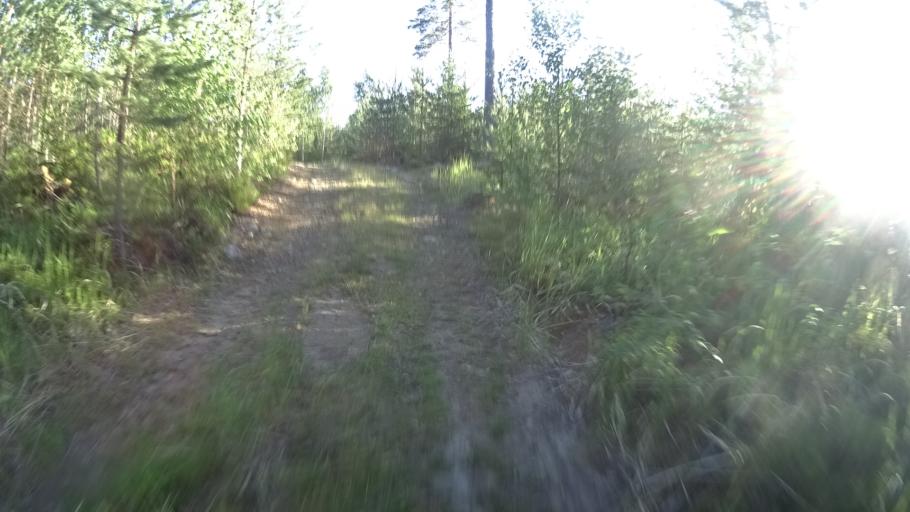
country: FI
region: Uusimaa
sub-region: Helsinki
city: Karkkila
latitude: 60.5954
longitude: 24.1062
